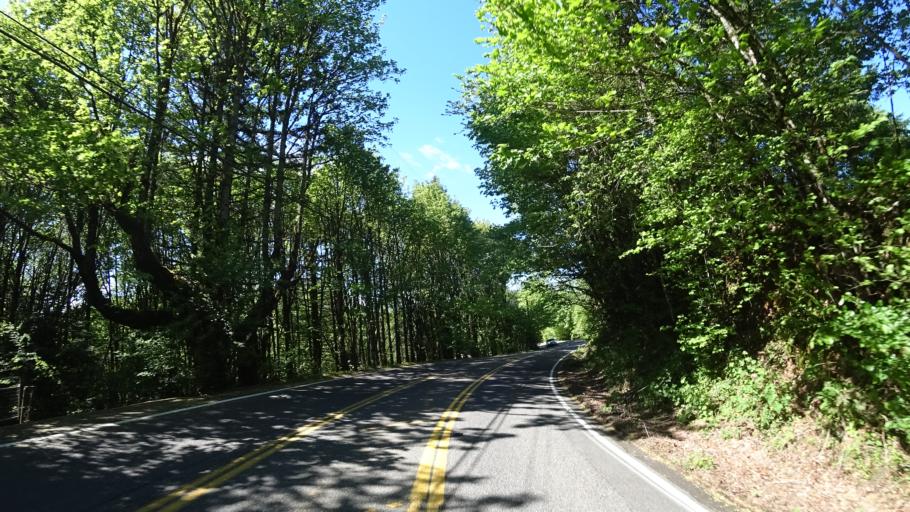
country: US
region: Oregon
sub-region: Washington County
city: Cedar Mill
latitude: 45.5600
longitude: -122.7847
